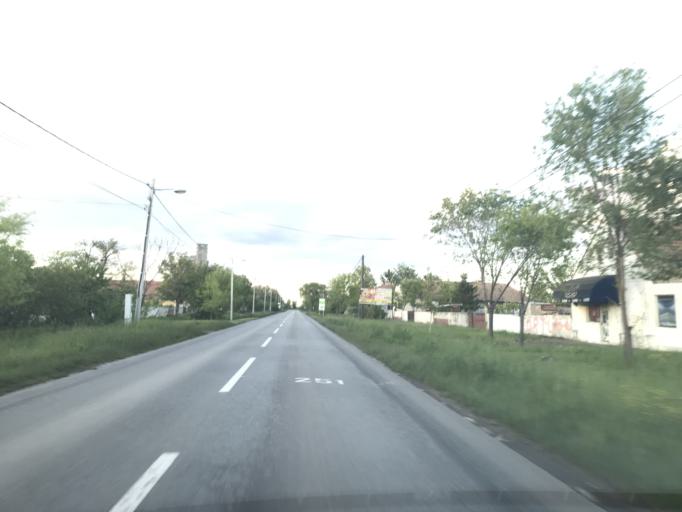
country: RS
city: Cestereg
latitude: 45.5661
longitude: 20.5358
